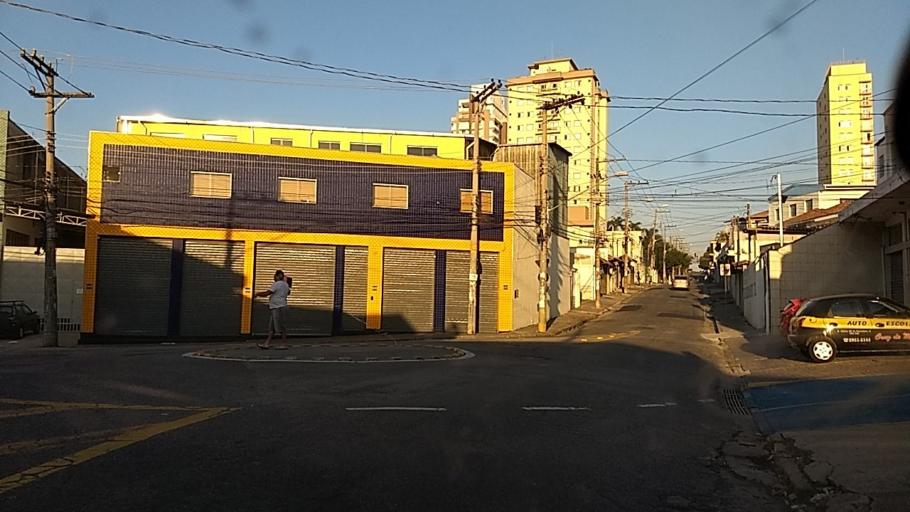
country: BR
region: Sao Paulo
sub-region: Sao Paulo
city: Sao Paulo
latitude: -23.4918
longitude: -46.5993
